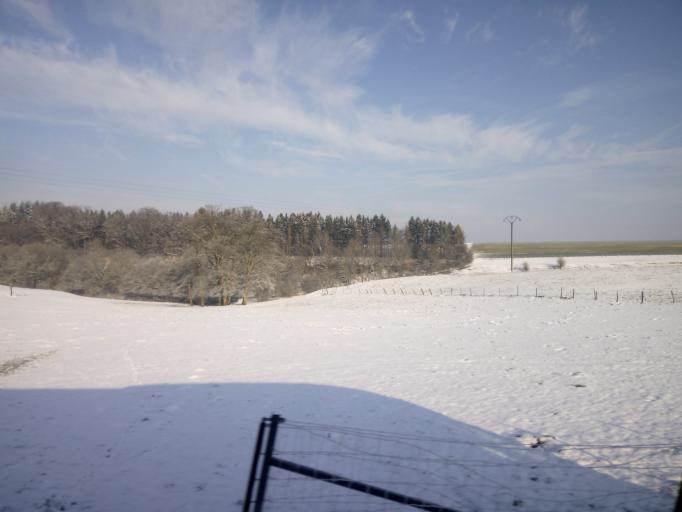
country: LU
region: Grevenmacher
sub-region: Canton d'Echternach
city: Consdorf
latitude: 49.7592
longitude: 6.3332
